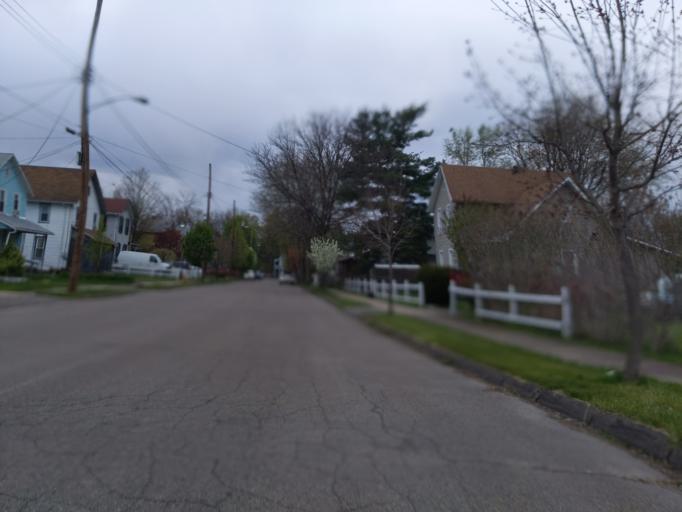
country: US
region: New York
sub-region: Chemung County
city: Elmira
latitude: 42.0720
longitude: -76.8029
